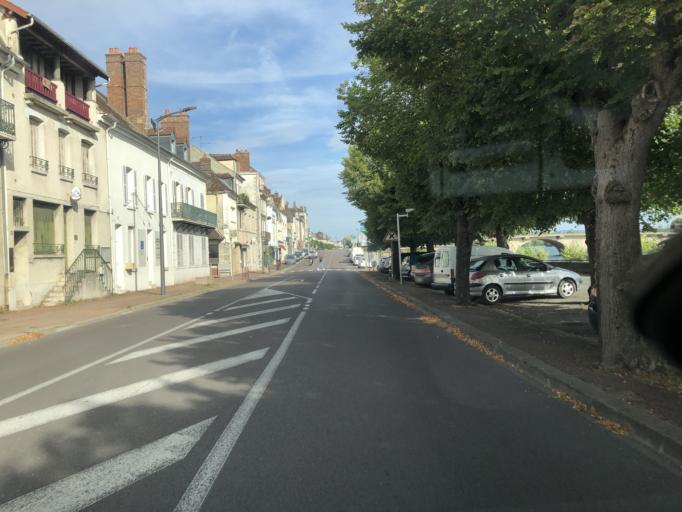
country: FR
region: Bourgogne
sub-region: Departement de l'Yonne
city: Joigny
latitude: 47.9821
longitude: 3.3932
